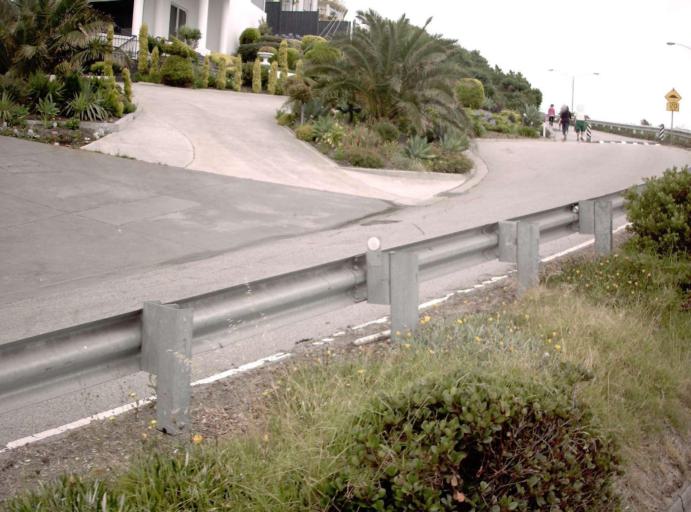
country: AU
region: Victoria
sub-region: Frankston
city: Frankston
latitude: -38.1546
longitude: 145.1076
